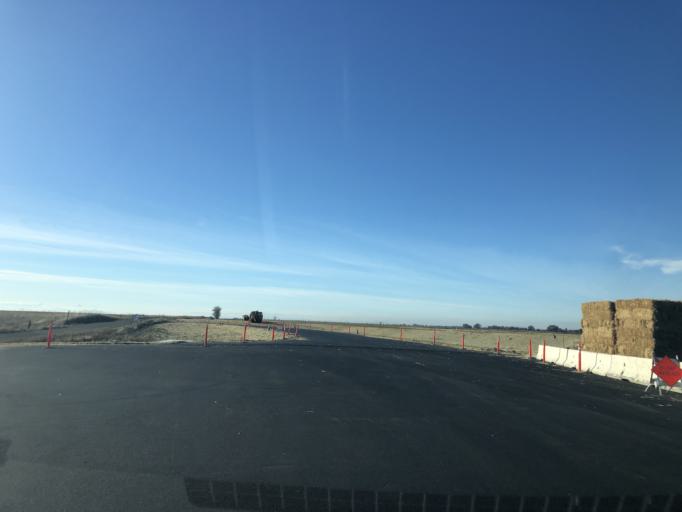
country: US
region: California
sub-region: Sacramento County
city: Antelope
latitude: 38.7954
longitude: -121.3873
